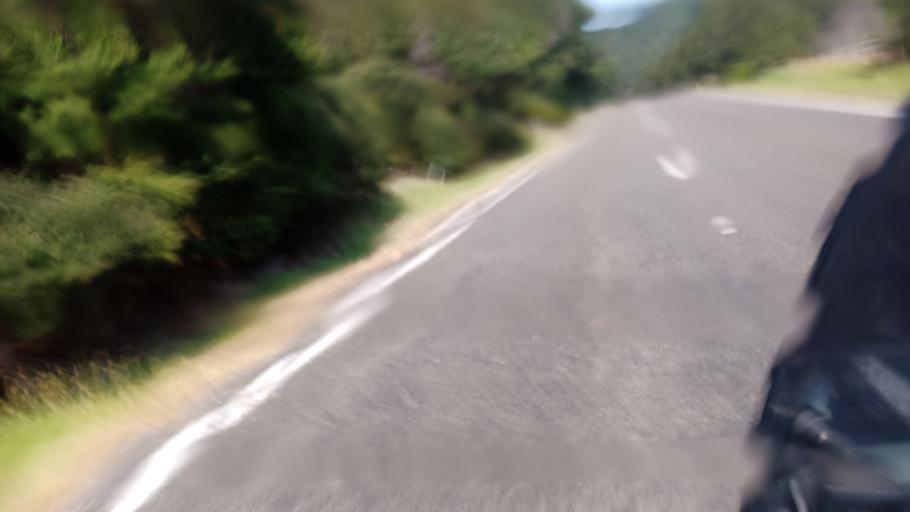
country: NZ
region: Bay of Plenty
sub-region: Opotiki District
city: Opotiki
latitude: -37.6043
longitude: 178.2691
